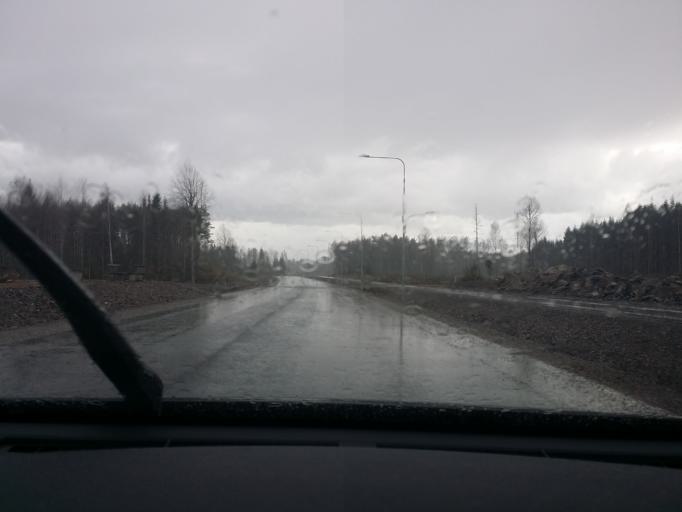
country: SE
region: Soedermanland
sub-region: Eskilstuna Kommun
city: Arla
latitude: 59.3632
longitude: 16.6998
